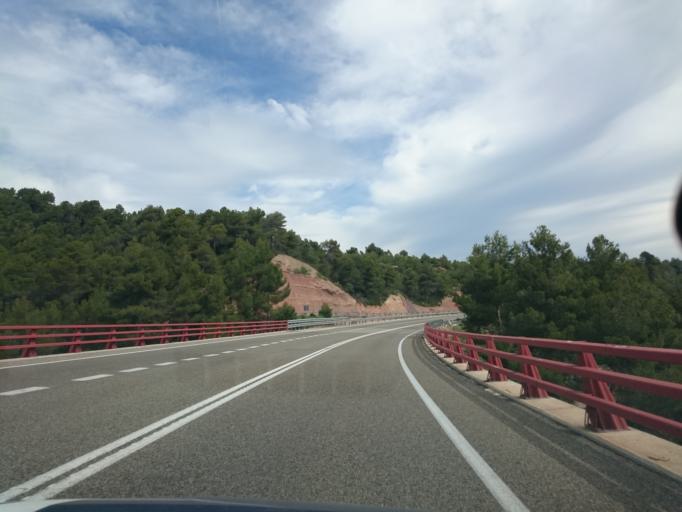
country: ES
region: Catalonia
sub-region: Provincia de Barcelona
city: Castellfollit del Boix
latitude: 41.6514
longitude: 1.7072
